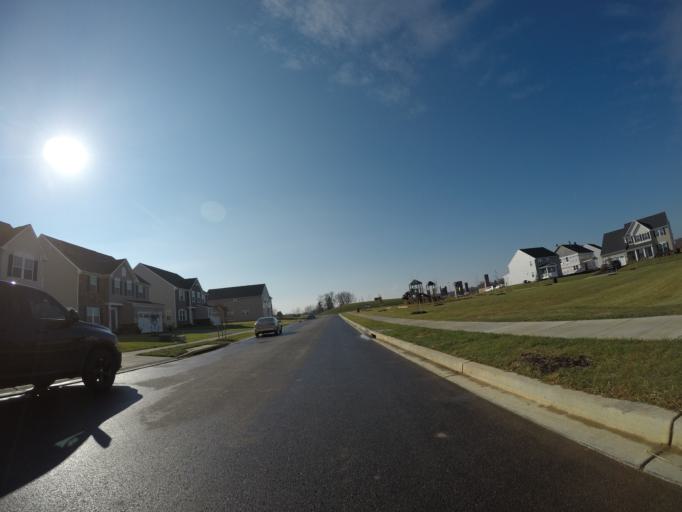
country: US
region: Maryland
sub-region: Frederick County
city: Ballenger Creek
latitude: 39.3782
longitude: -77.4406
